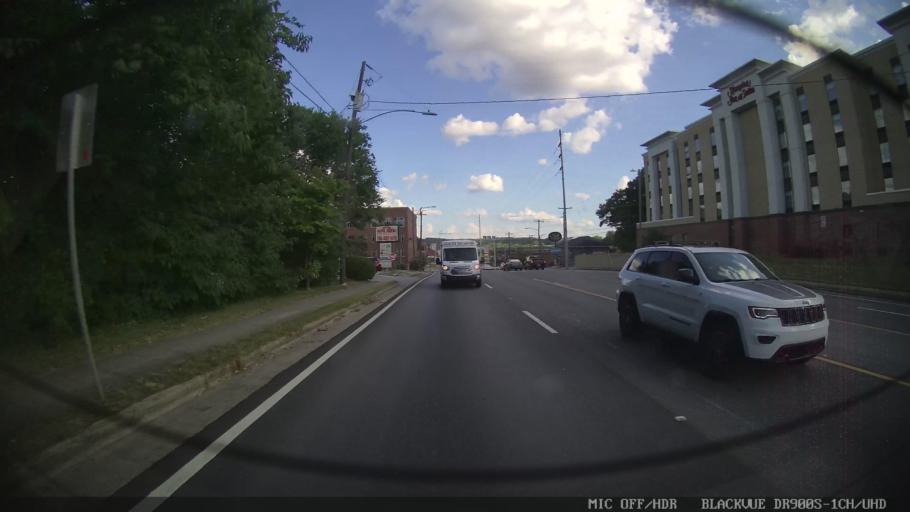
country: US
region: Georgia
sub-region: Floyd County
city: Rome
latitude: 34.2587
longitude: -85.1651
